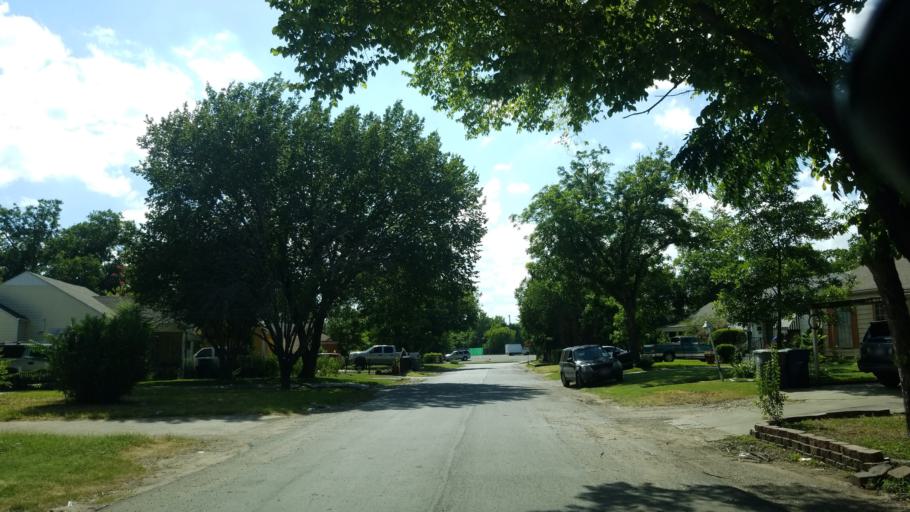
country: US
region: Texas
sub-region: Dallas County
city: Balch Springs
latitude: 32.7722
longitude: -96.7037
